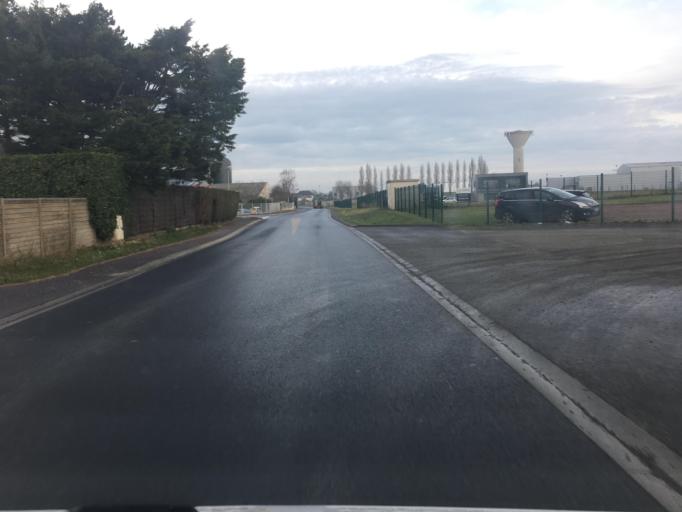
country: FR
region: Lower Normandy
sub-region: Departement du Calvados
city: Creully
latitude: 49.2740
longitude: -0.5465
